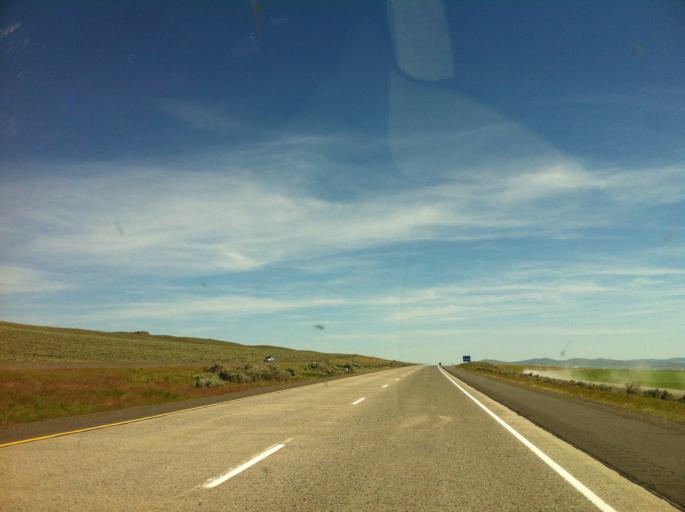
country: US
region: Oregon
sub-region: Union County
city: Union
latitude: 45.1026
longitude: -117.9555
